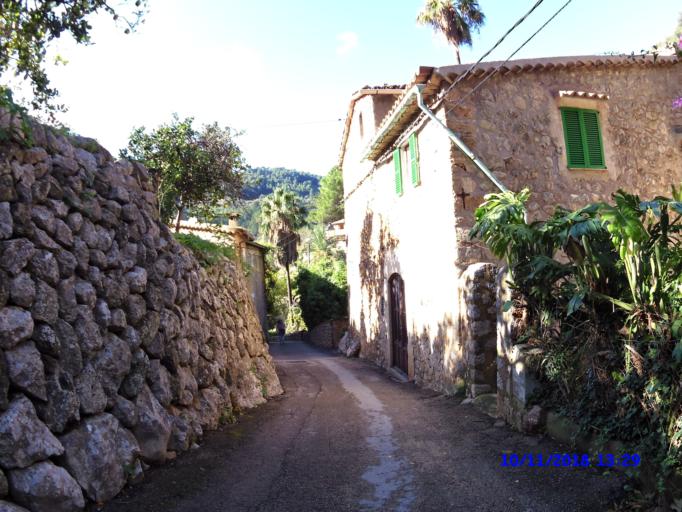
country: ES
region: Balearic Islands
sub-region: Illes Balears
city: Deia
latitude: 39.7467
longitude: 2.6473
